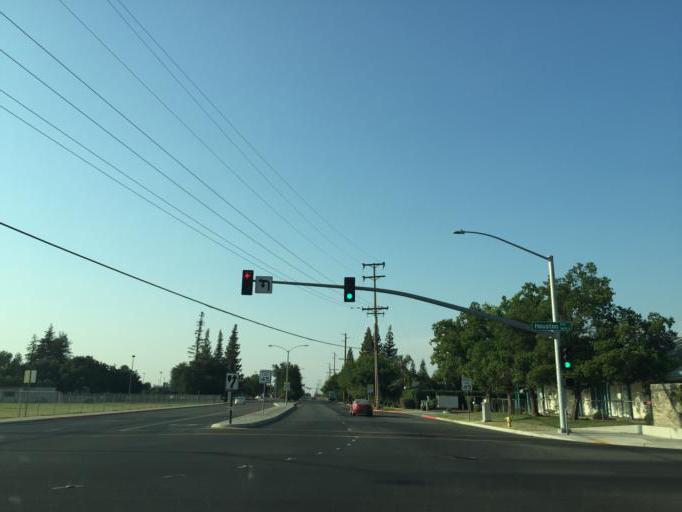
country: US
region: California
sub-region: Tulare County
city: Visalia
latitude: 36.3419
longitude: -119.2520
